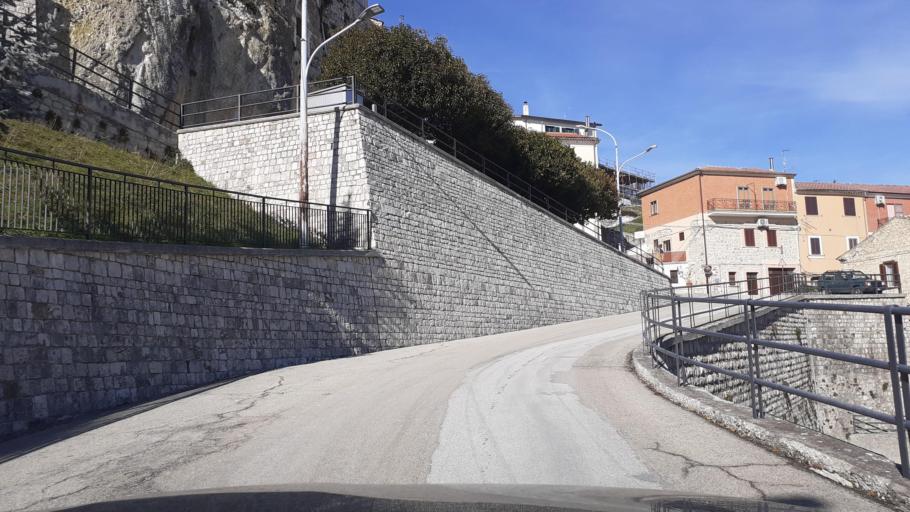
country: IT
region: Molise
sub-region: Provincia di Campobasso
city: Pietracupa
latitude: 41.6821
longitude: 14.5209
